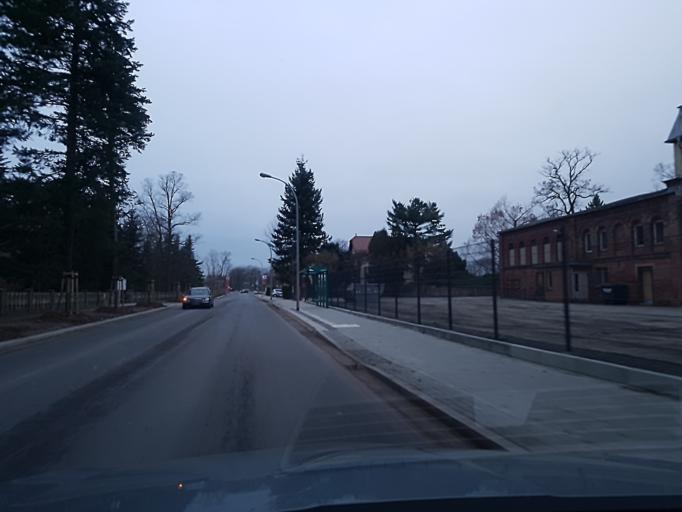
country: DE
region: Brandenburg
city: Finsterwalde
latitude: 51.6412
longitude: 13.6994
